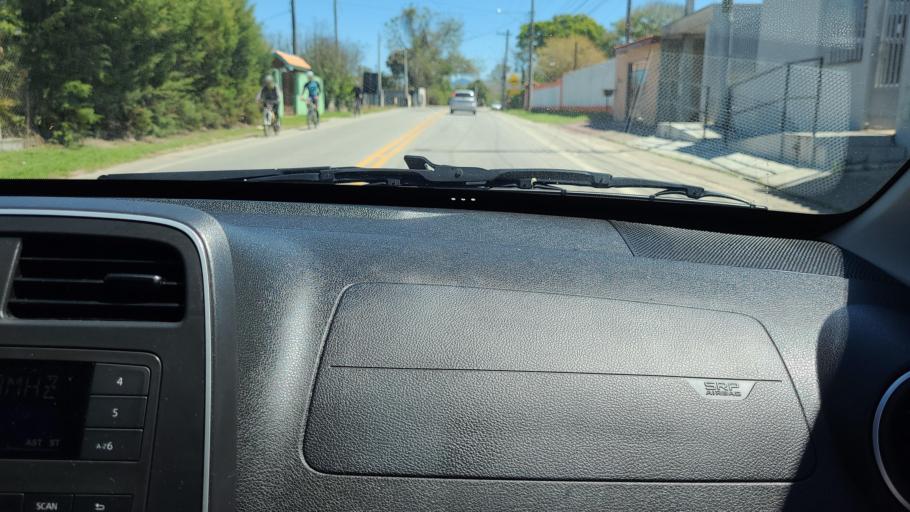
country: BR
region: Sao Paulo
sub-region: Tremembe
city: Tremembe
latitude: -22.8854
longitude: -45.5313
